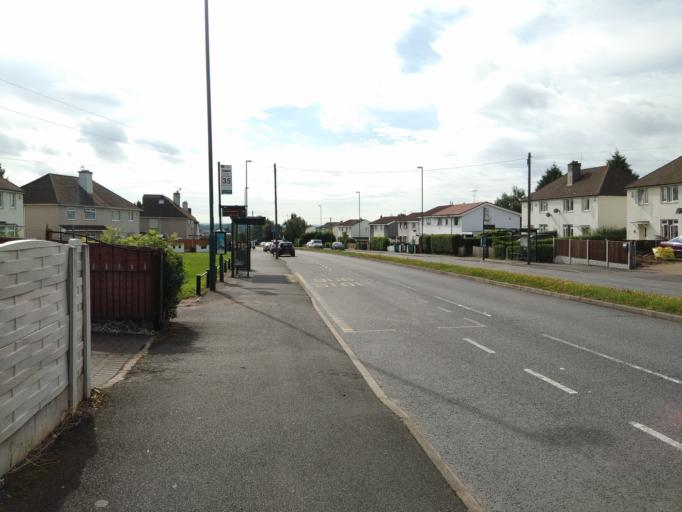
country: GB
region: England
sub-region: Nottinghamshire
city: Kimberley
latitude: 52.9701
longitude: -1.2282
